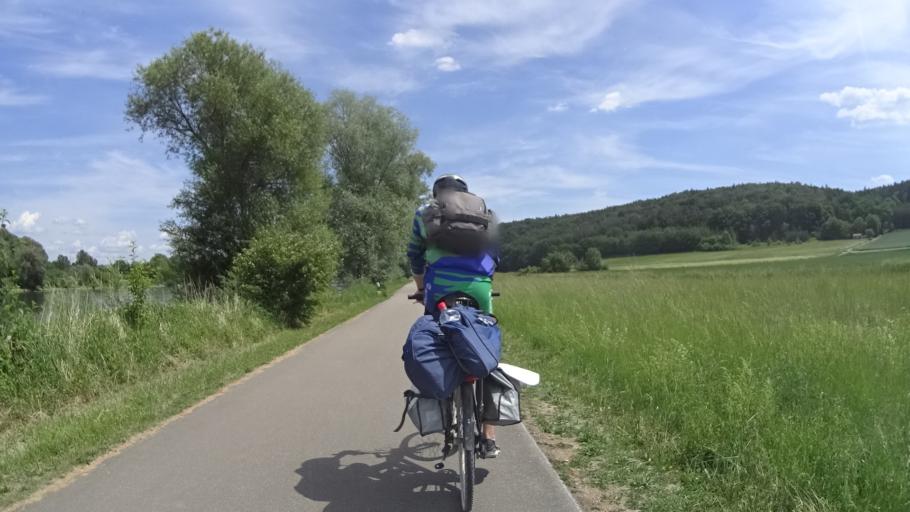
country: DE
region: Bavaria
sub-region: Upper Palatinate
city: Sinzing
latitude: 48.9680
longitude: 12.0177
